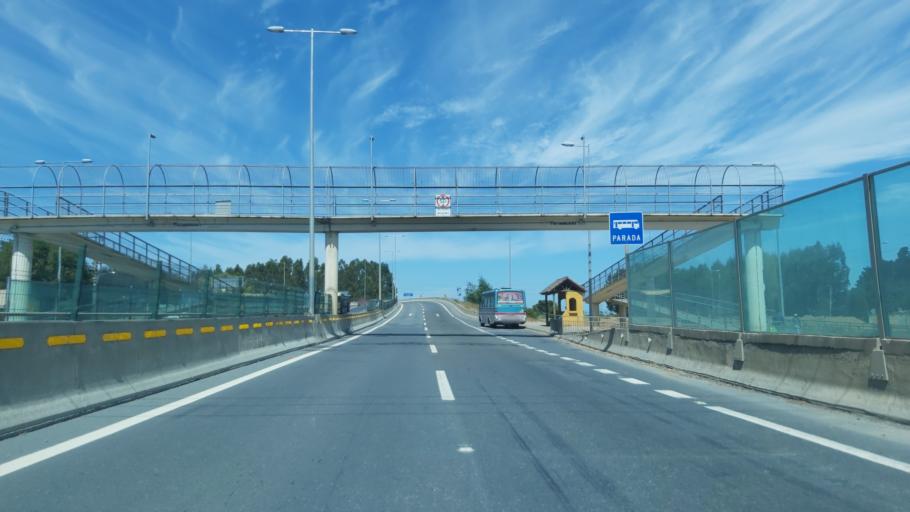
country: CL
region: Biobio
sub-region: Provincia de Concepcion
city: Lota
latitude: -37.1099
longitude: -73.1460
